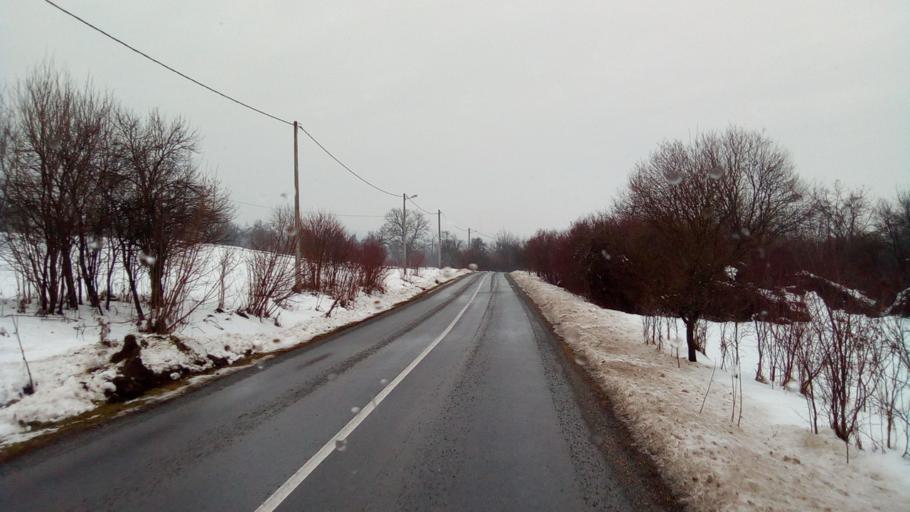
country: HR
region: Sisacko-Moslavacka
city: Petrinja
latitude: 45.3919
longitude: 16.2960
